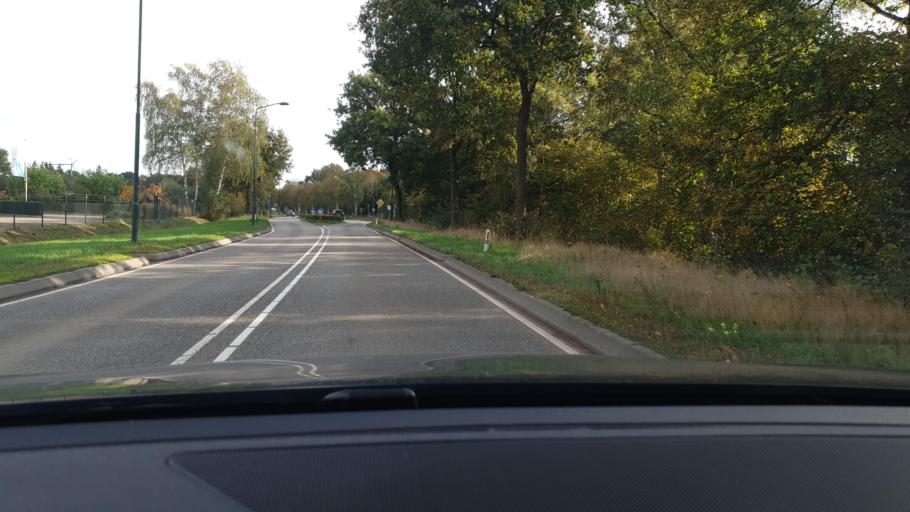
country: NL
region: North Brabant
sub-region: Gemeente Veghel
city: Veghel
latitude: 51.6109
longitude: 5.5584
